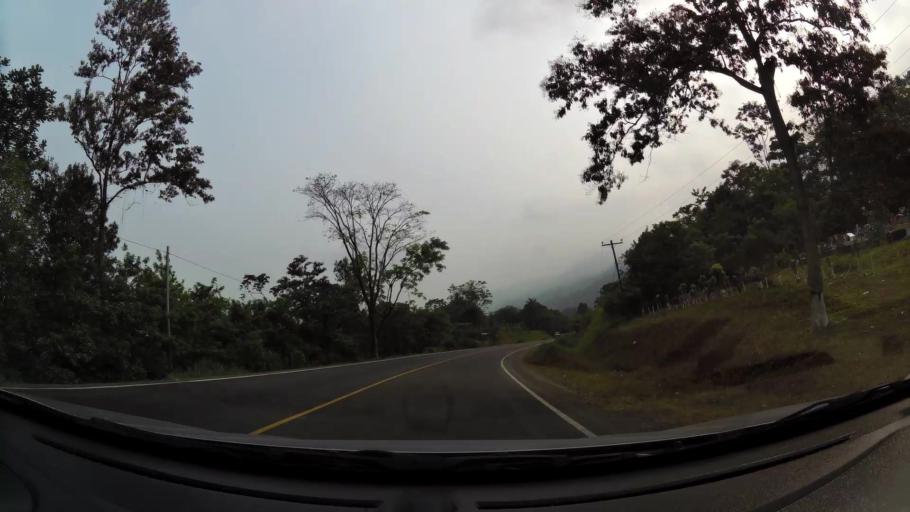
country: HN
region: Atlantida
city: Mezapa
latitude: 15.5892
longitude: -87.6114
